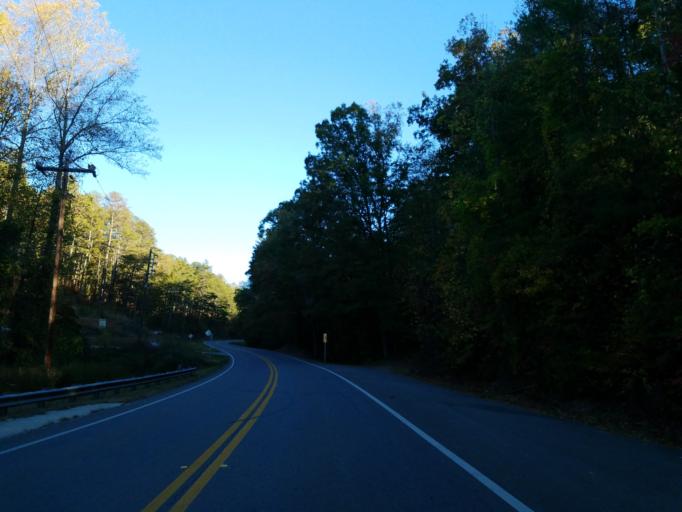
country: US
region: Georgia
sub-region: Dawson County
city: Dawsonville
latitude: 34.4261
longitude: -84.2121
